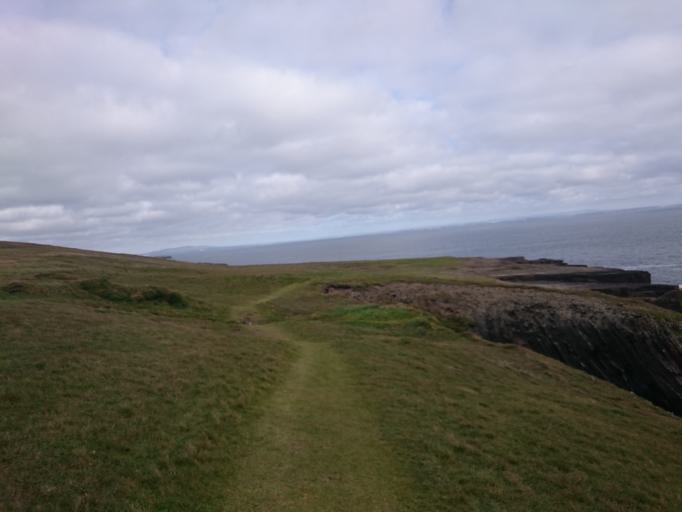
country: IE
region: Munster
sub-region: Ciarrai
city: Ballybunnion
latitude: 52.5579
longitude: -9.9318
